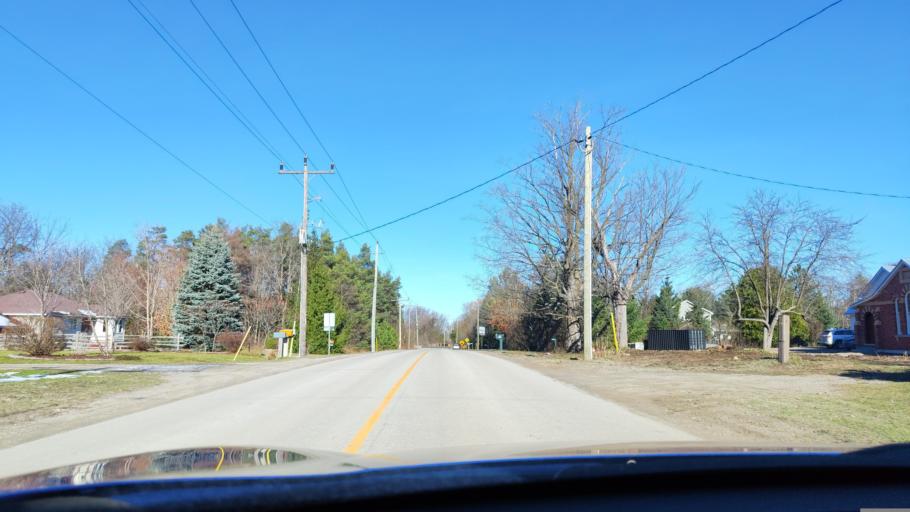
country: CA
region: Ontario
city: Collingwood
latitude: 44.4635
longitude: -80.1735
